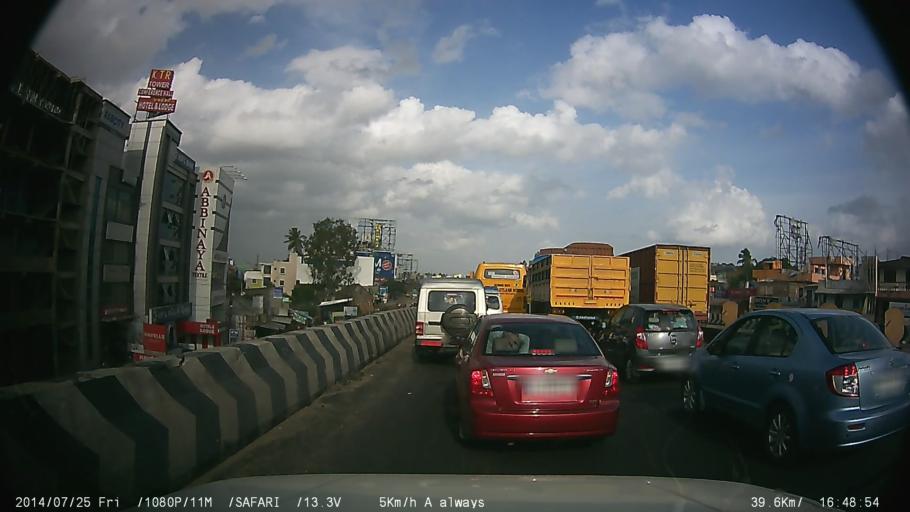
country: IN
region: Tamil Nadu
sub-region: Krishnagiri
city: Hosur
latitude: 12.7348
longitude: 77.8307
